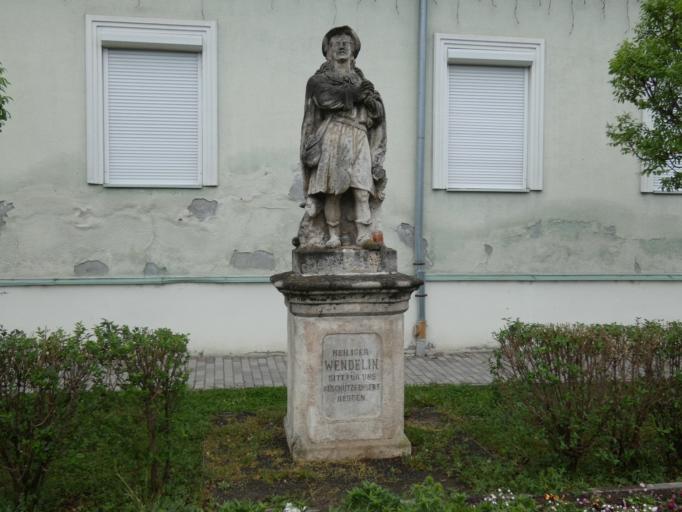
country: HU
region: Pest
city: Biatorbagy
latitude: 47.4778
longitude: 18.8291
